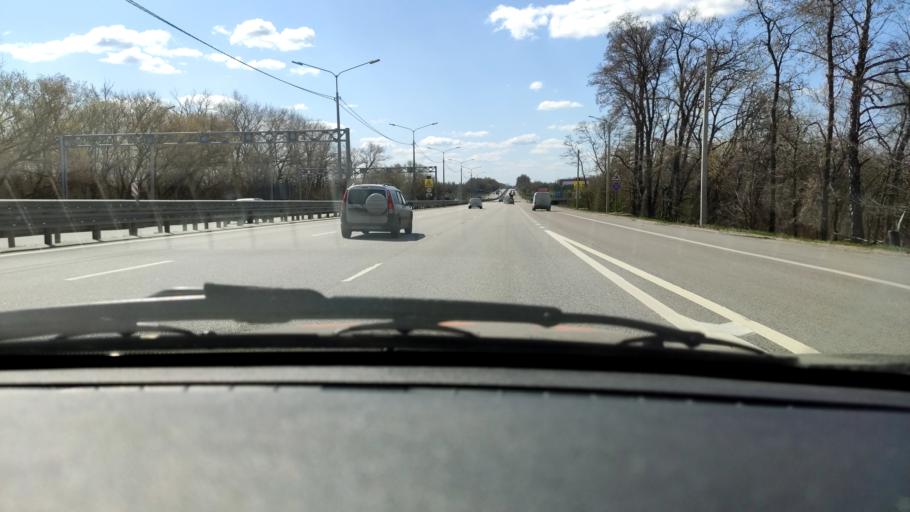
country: RU
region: Voronezj
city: Podgornoye
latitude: 51.8301
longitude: 39.2120
